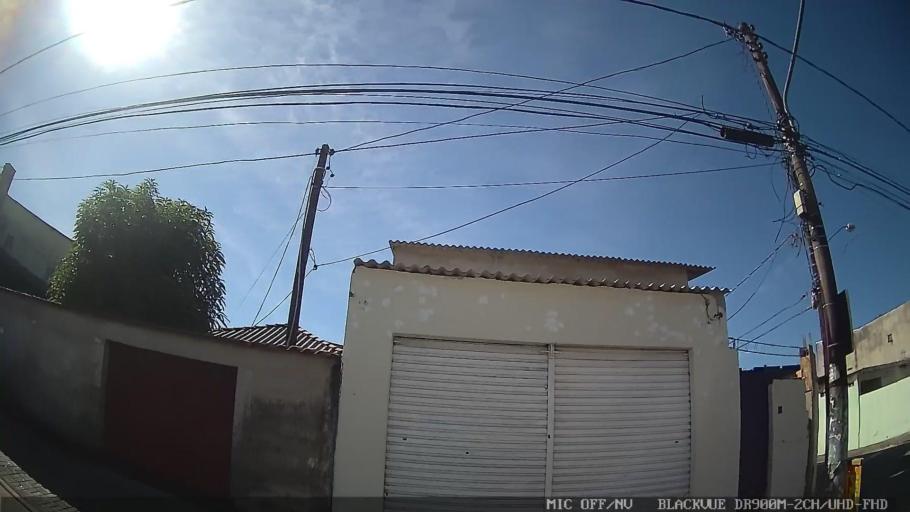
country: BR
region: Sao Paulo
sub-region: Santos
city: Santos
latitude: -23.9445
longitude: -46.2925
